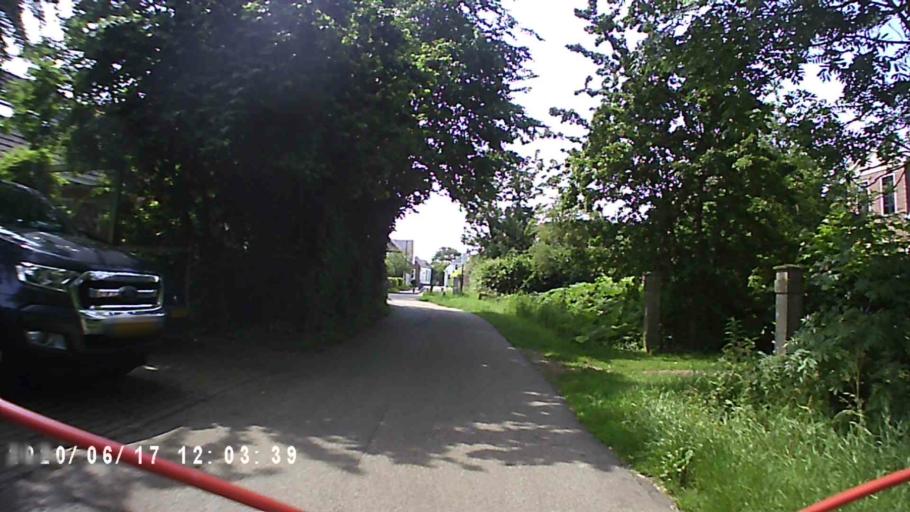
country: NL
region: Groningen
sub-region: Gemeente De Marne
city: Ulrum
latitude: 53.3376
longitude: 6.3427
